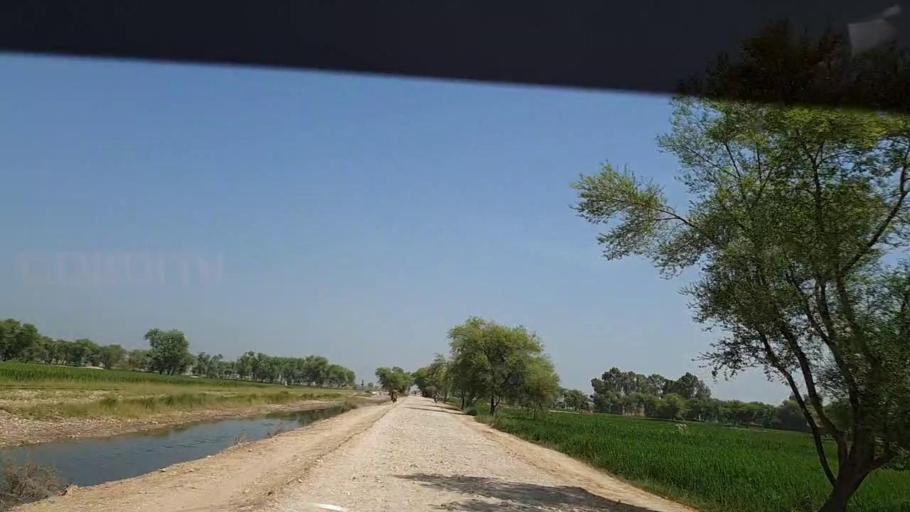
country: PK
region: Sindh
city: Tangwani
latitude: 28.2826
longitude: 69.0308
